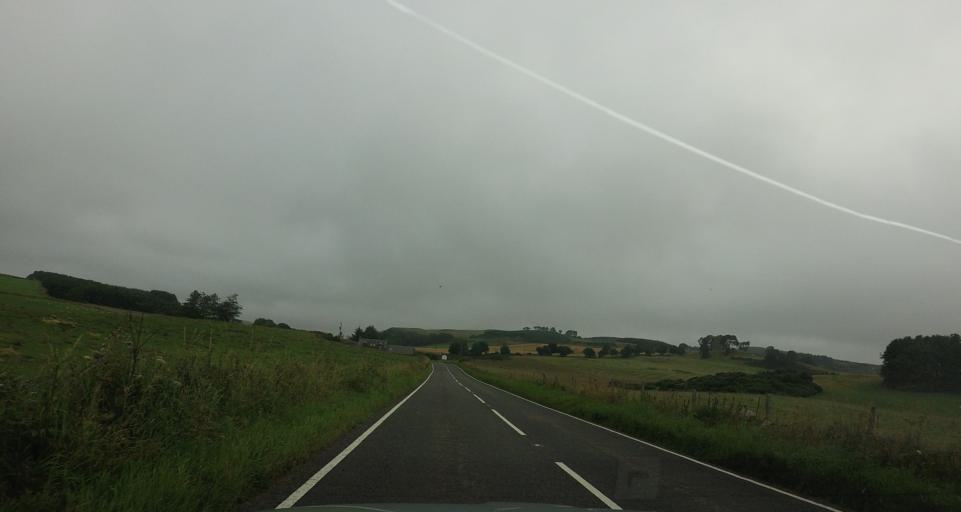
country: GB
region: Scotland
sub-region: Perth and Kinross
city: Abernethy
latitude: 56.2839
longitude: -3.3476
